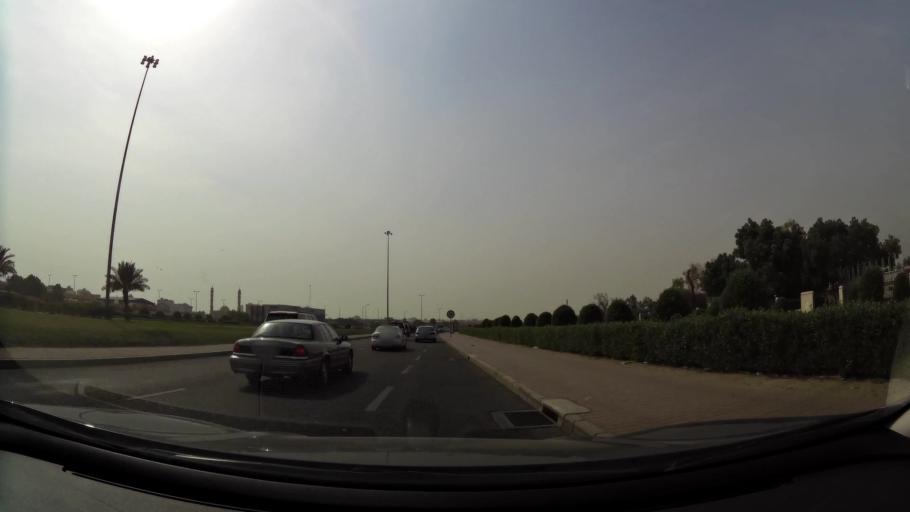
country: KW
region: Al Asimah
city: Ar Rabiyah
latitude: 29.2896
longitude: 47.9465
